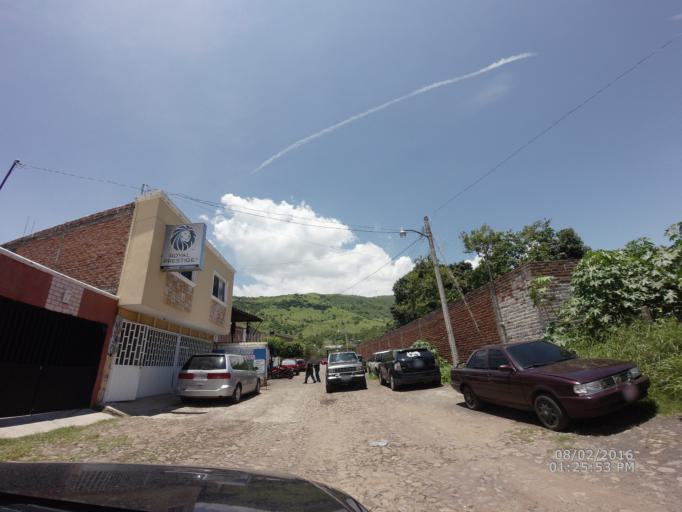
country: MX
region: Nayarit
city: Ixtlan del Rio
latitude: 21.0394
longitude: -104.3762
